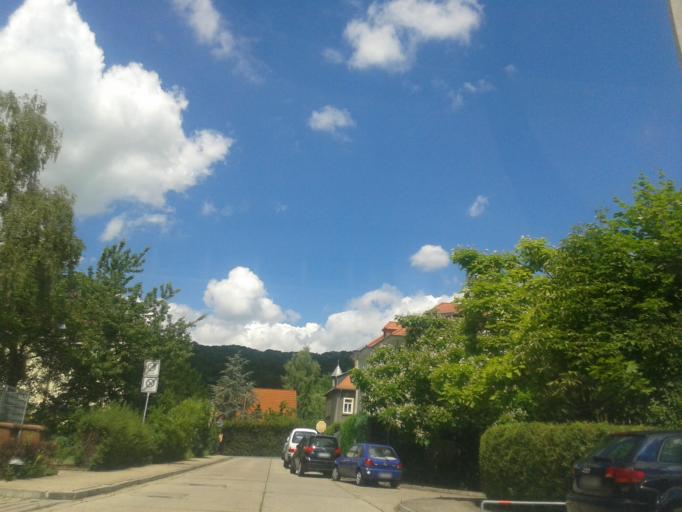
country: DE
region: Saxony
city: Radebeul
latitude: 51.1051
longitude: 13.6865
